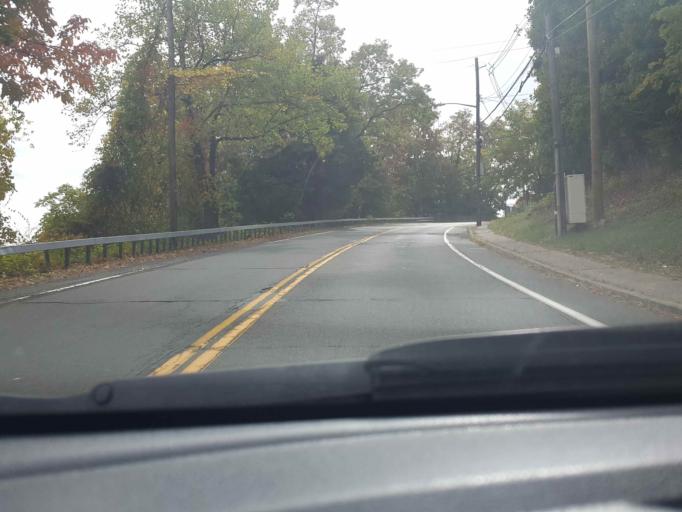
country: US
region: New York
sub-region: Rockland County
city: South Nyack
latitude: 41.0830
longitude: -73.9244
